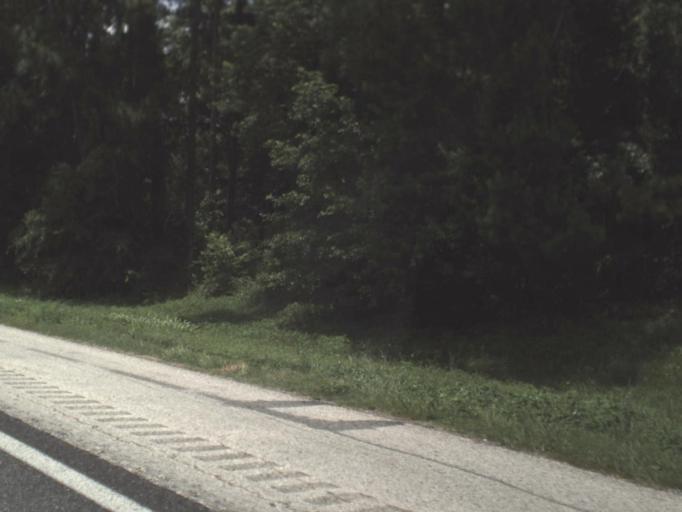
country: US
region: Florida
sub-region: Alachua County
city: High Springs
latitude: 29.8645
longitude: -82.5410
